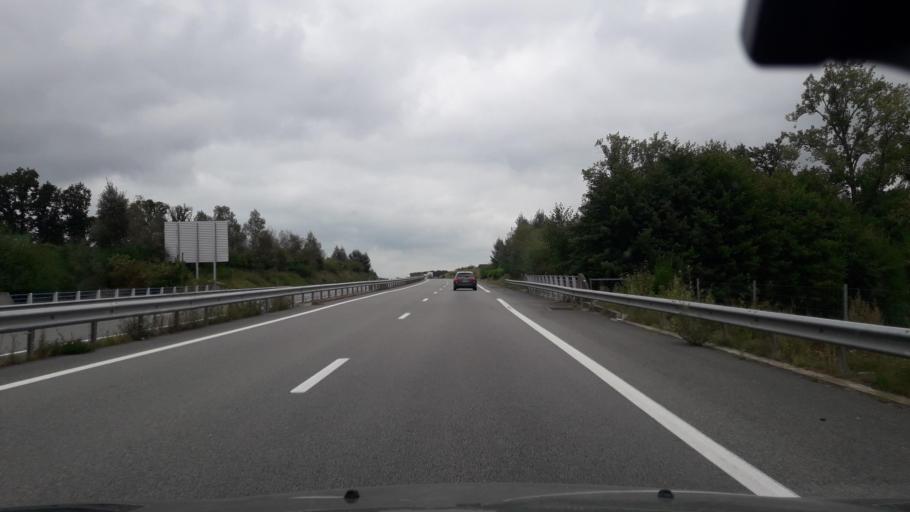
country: FR
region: Limousin
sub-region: Departement de la Creuse
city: Gouzon
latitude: 46.2052
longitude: 2.2673
